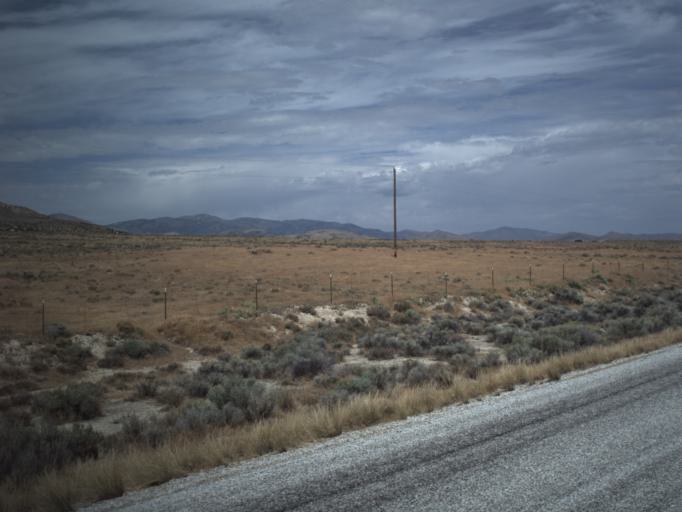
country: US
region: Utah
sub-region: Tooele County
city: Wendover
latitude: 41.5136
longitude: -113.5998
